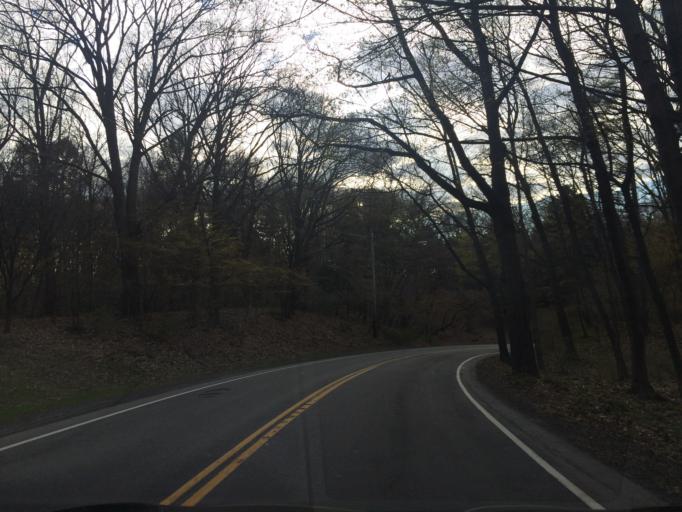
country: US
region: New York
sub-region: Monroe County
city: Irondequoit
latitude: 43.2277
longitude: -77.5518
